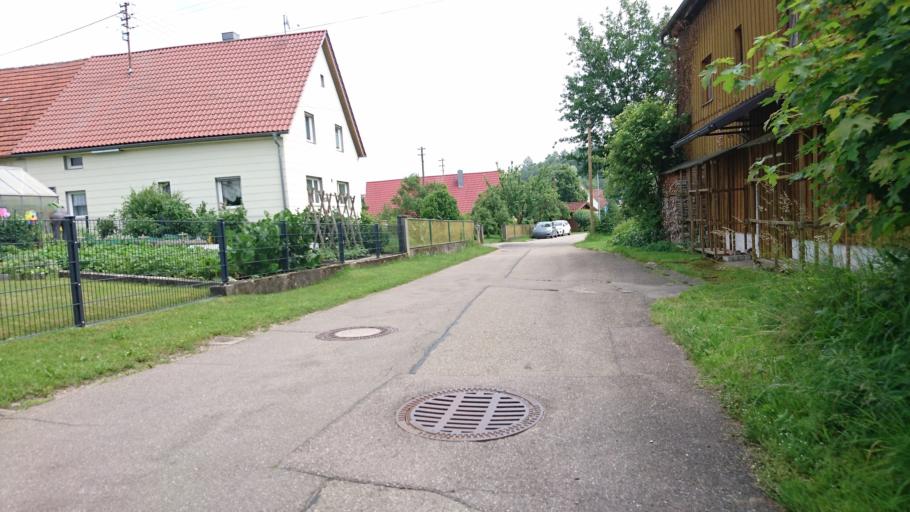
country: DE
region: Bavaria
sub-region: Swabia
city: Landensberg
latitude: 48.4328
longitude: 10.5037
